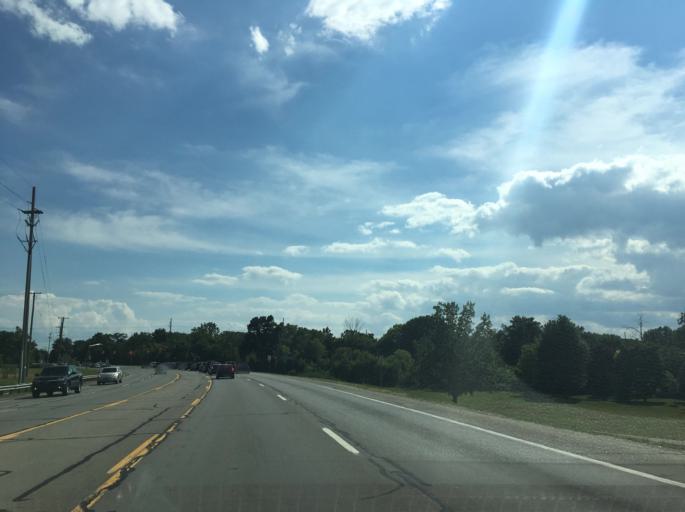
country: US
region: Michigan
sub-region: Macomb County
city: Clinton
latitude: 42.5898
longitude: -82.9022
